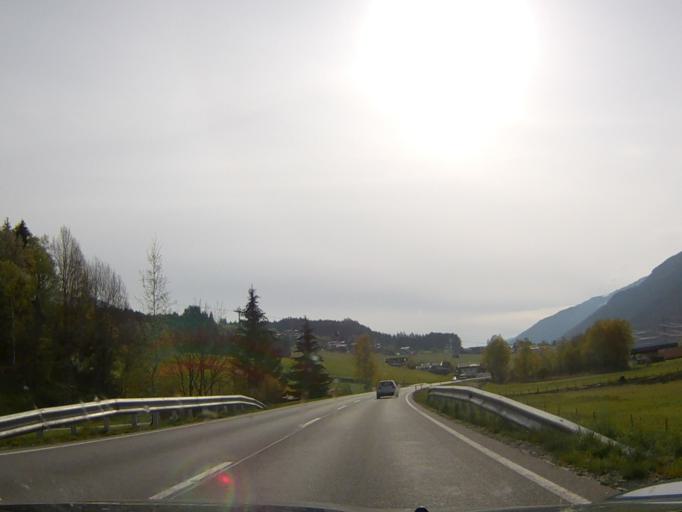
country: AT
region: Salzburg
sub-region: Politischer Bezirk Zell am See
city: Hollersbach im Pinzgau
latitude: 47.2798
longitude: 12.3926
